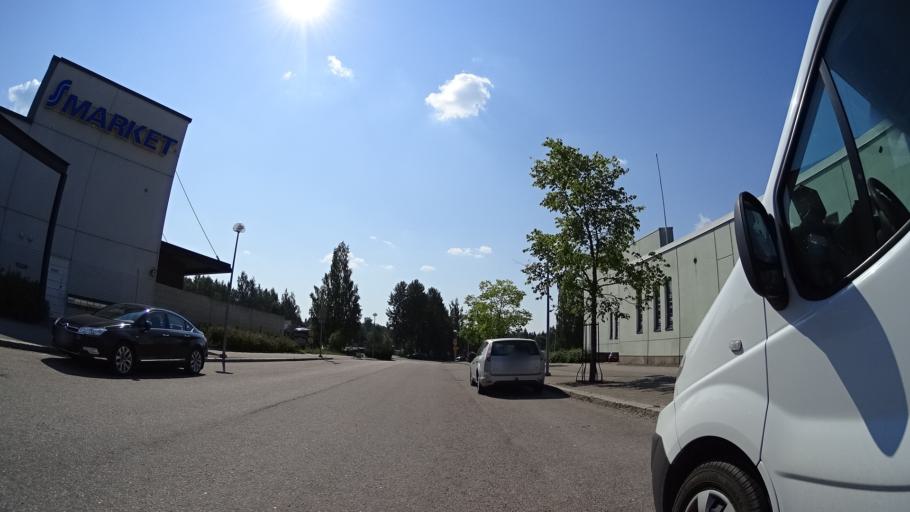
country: FI
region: Uusimaa
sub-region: Helsinki
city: Kerava
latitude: 60.3485
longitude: 25.0750
